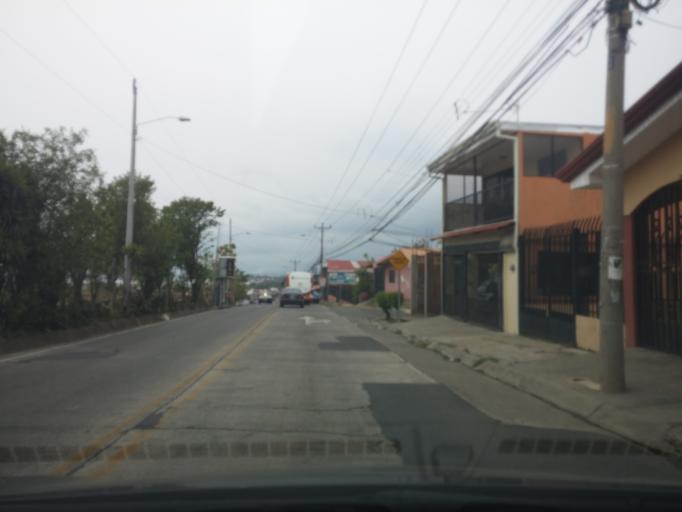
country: CR
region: Heredia
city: Llorente
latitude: 9.9924
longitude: -84.1470
